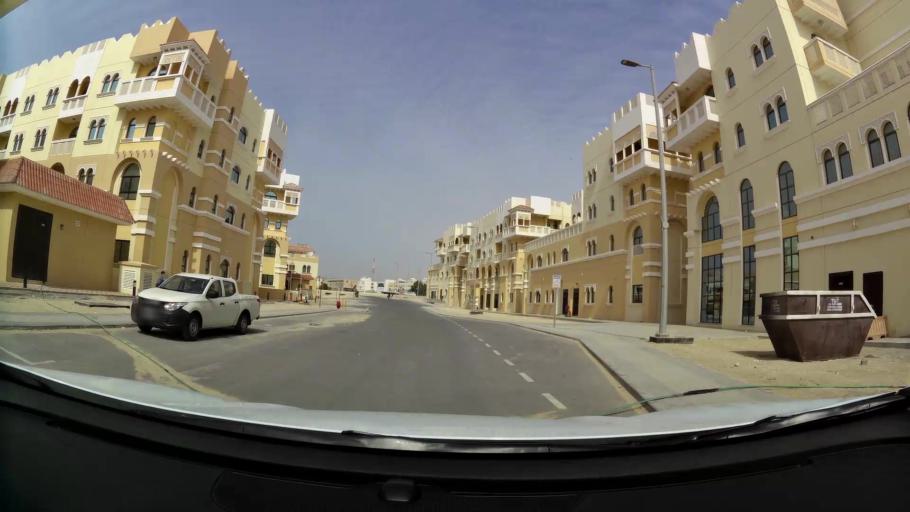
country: AE
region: Abu Dhabi
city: Abu Dhabi
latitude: 24.5508
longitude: 54.6923
